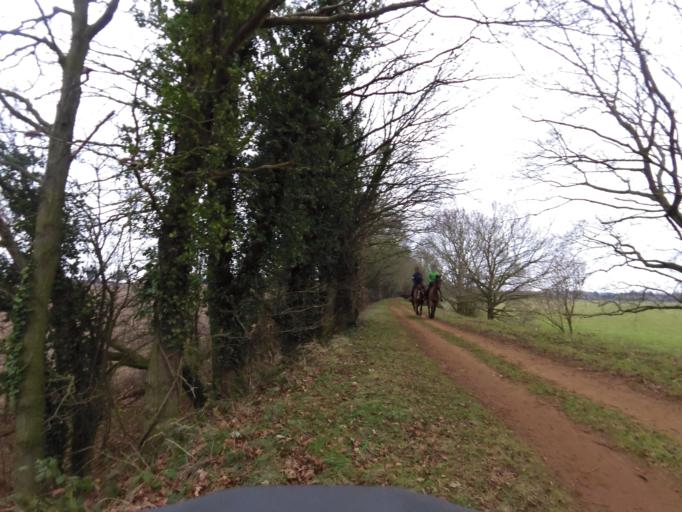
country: GB
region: England
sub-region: Norfolk
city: Costessey
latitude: 52.7153
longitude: 1.1449
